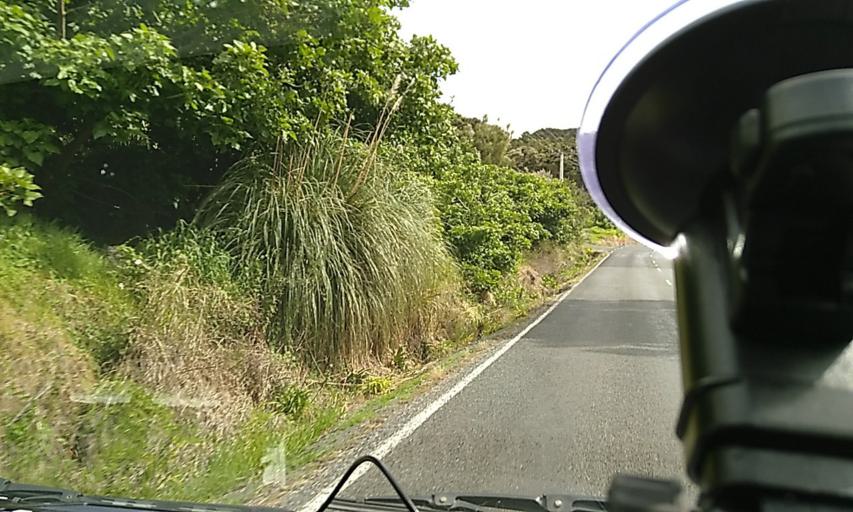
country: NZ
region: Northland
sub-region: Far North District
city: Ahipara
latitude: -35.5362
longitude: 173.3869
